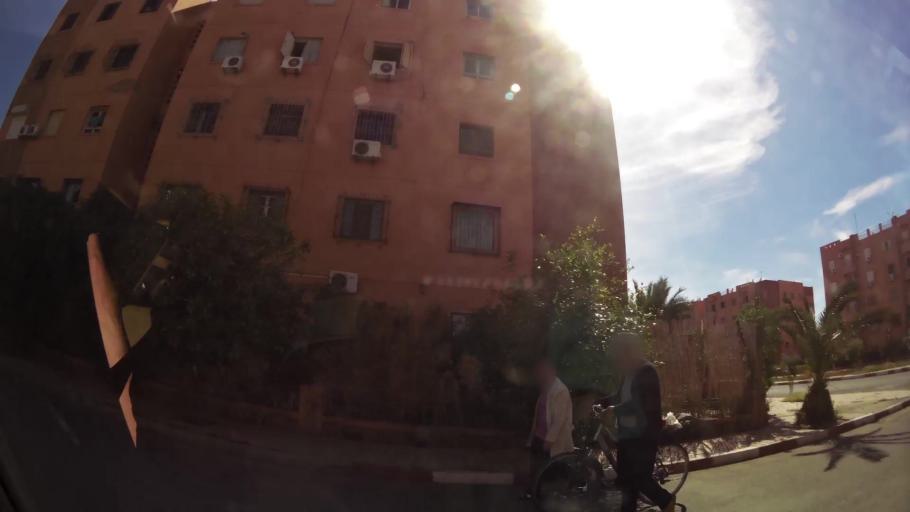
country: MA
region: Marrakech-Tensift-Al Haouz
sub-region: Marrakech
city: Marrakesh
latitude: 31.6657
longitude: -8.0310
